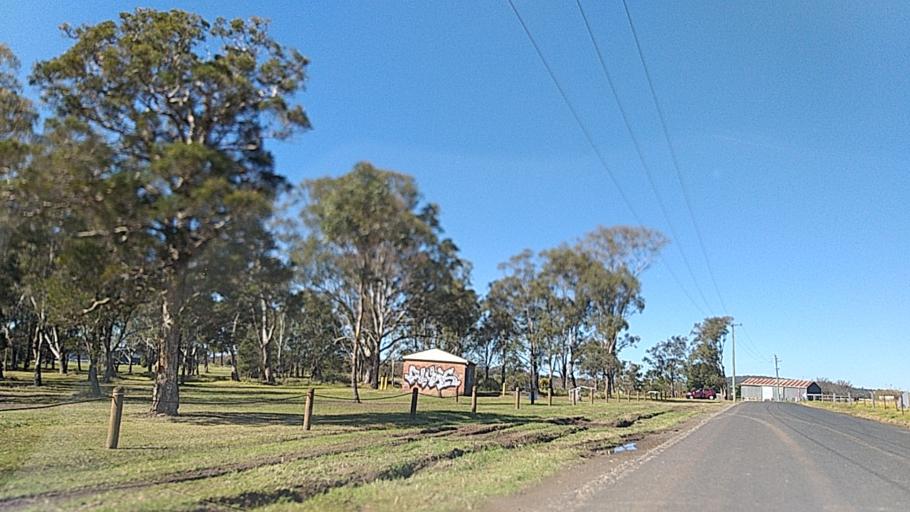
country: AU
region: New South Wales
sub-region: Wollongong
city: Dapto
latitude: -34.4775
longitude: 150.7914
